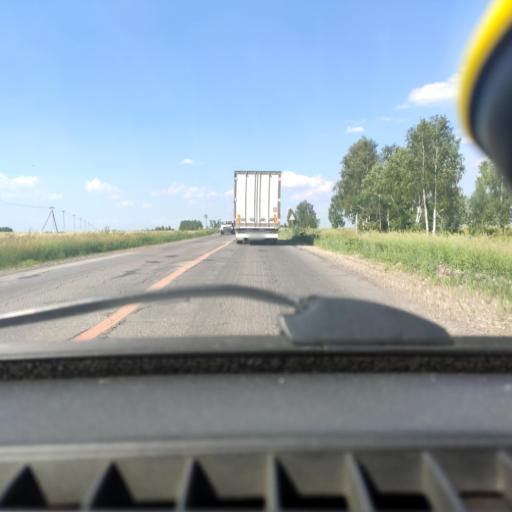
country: RU
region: Samara
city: Povolzhskiy
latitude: 53.7221
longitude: 49.7512
